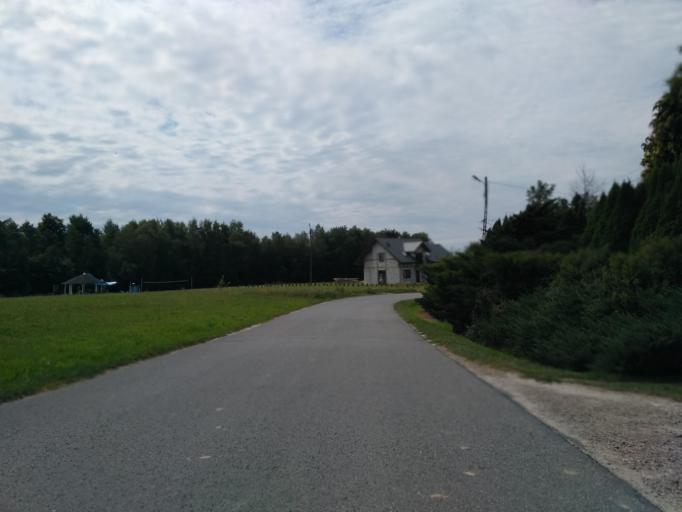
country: PL
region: Subcarpathian Voivodeship
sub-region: Powiat rzeszowski
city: Chmielnik
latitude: 49.9507
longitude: 22.1428
